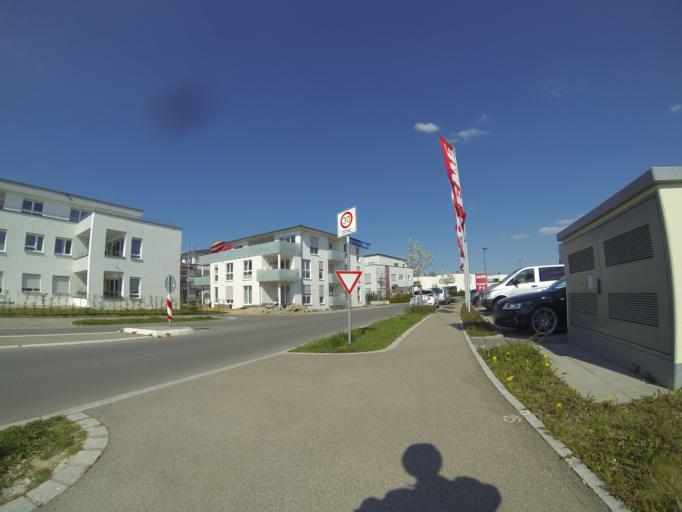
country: DE
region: Baden-Wuerttemberg
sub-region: Tuebingen Region
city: Laupheim
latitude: 48.2234
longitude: 9.8931
